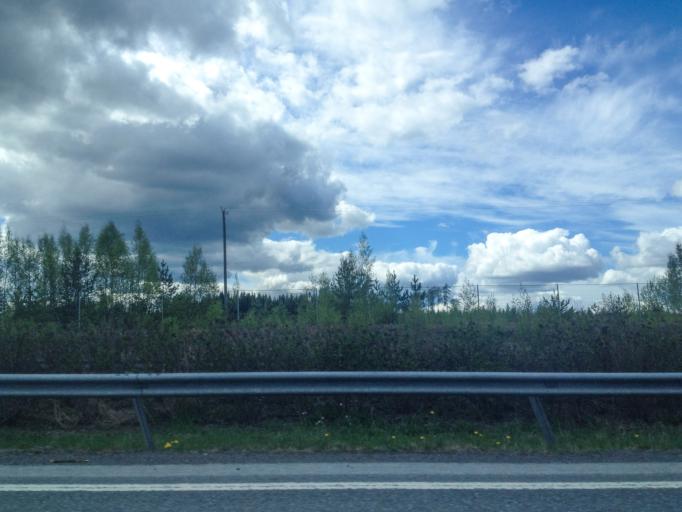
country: FI
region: Pirkanmaa
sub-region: Etelae-Pirkanmaa
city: Toijala
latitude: 61.2245
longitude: 23.8388
